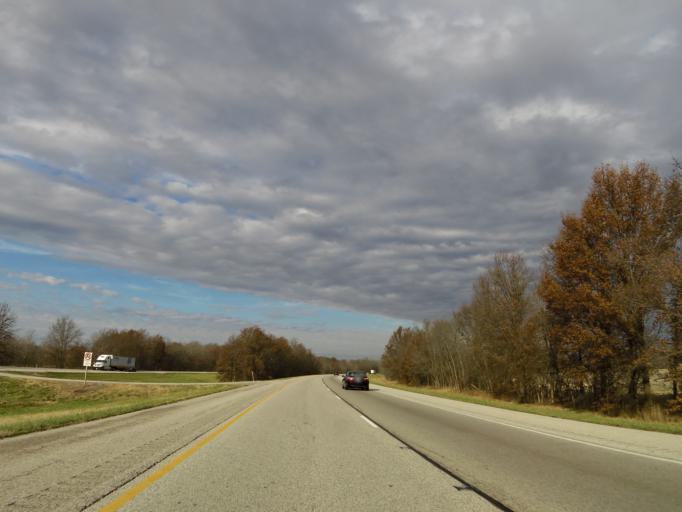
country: US
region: Illinois
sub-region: Washington County
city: Nashville
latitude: 38.3935
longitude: -89.3834
